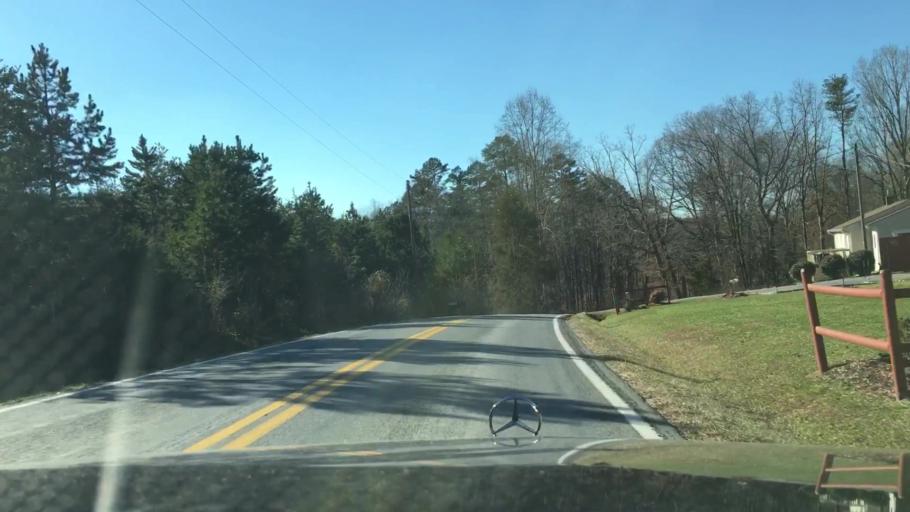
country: US
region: Virginia
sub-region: Pittsylvania County
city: Motley
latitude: 37.1529
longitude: -79.3717
